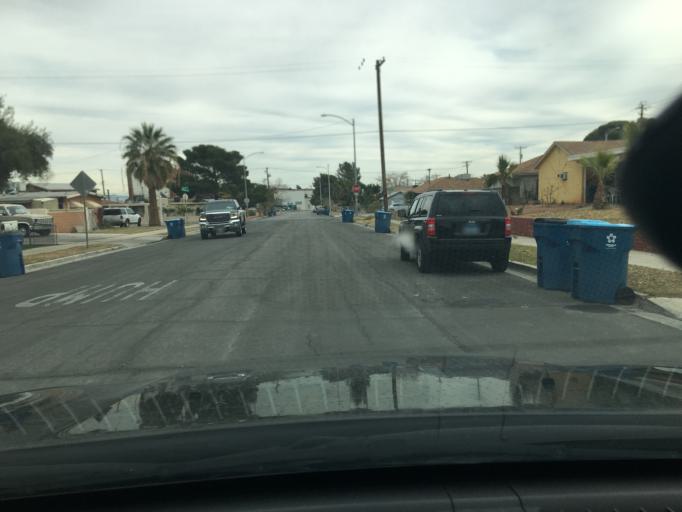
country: US
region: Nevada
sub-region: Clark County
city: Spring Valley
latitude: 36.1632
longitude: -115.2111
